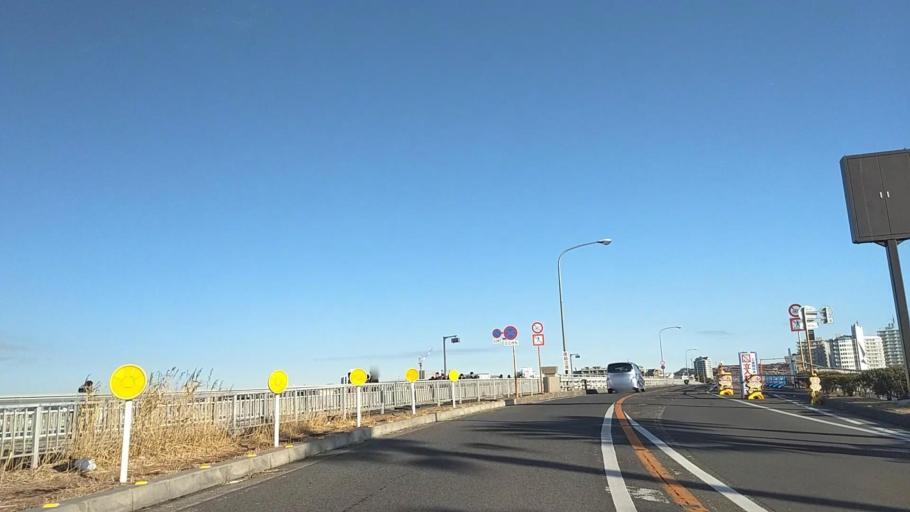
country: JP
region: Kanagawa
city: Fujisawa
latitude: 35.3026
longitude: 139.4815
